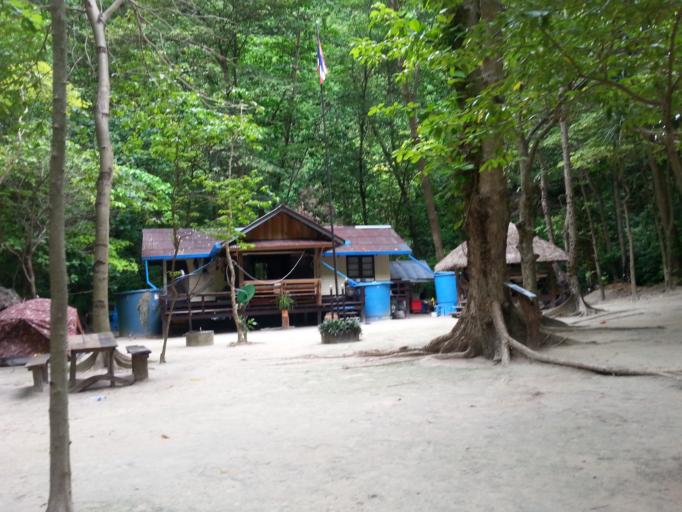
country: TH
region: Krabi
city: Saladan
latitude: 7.6751
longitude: 98.7660
